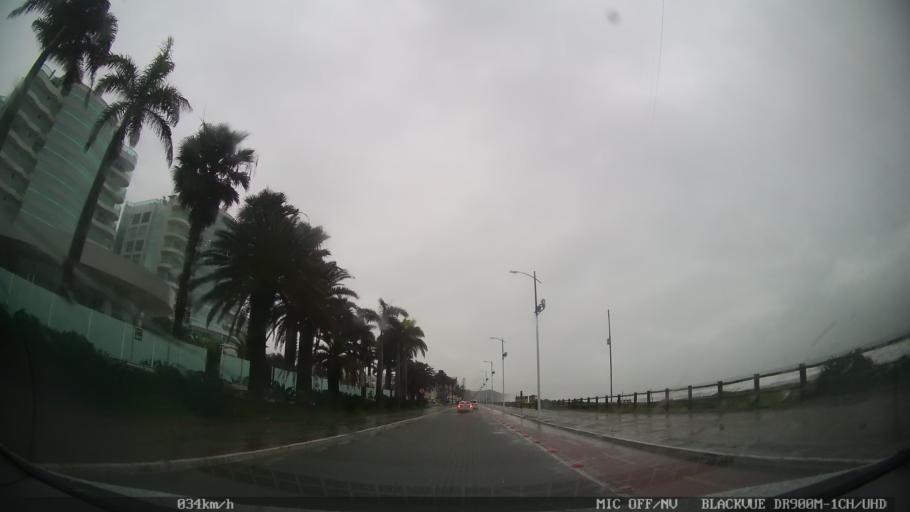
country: BR
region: Santa Catarina
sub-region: Balneario Camboriu
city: Balneario Camboriu
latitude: -26.9528
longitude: -48.6297
